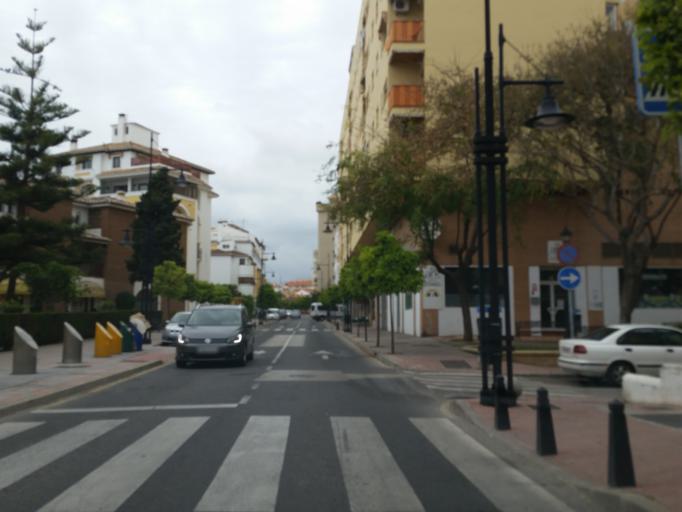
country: ES
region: Andalusia
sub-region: Provincia de Malaga
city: Fuengirola
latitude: 36.5456
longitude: -4.6234
